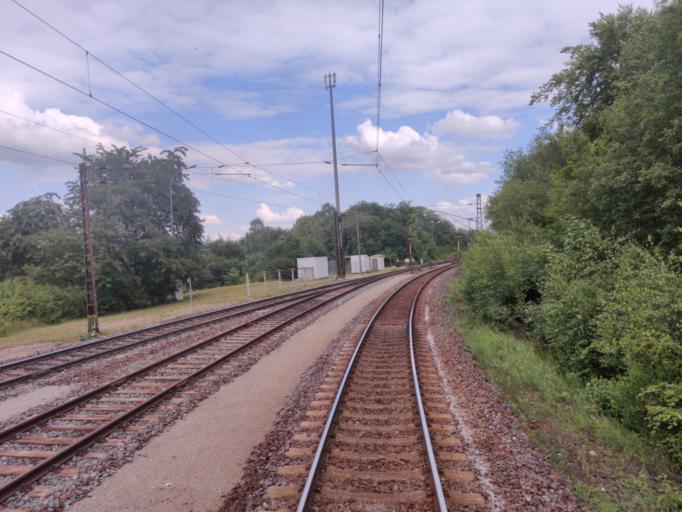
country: DE
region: Saxony-Anhalt
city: Huttenrode
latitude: 51.7987
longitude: 10.9214
